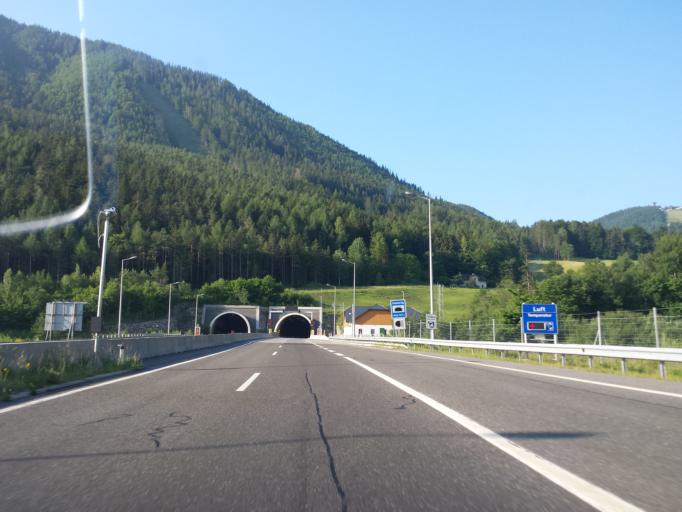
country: AT
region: Lower Austria
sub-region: Politischer Bezirk Neunkirchen
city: Semmering
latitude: 47.6405
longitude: 15.8498
